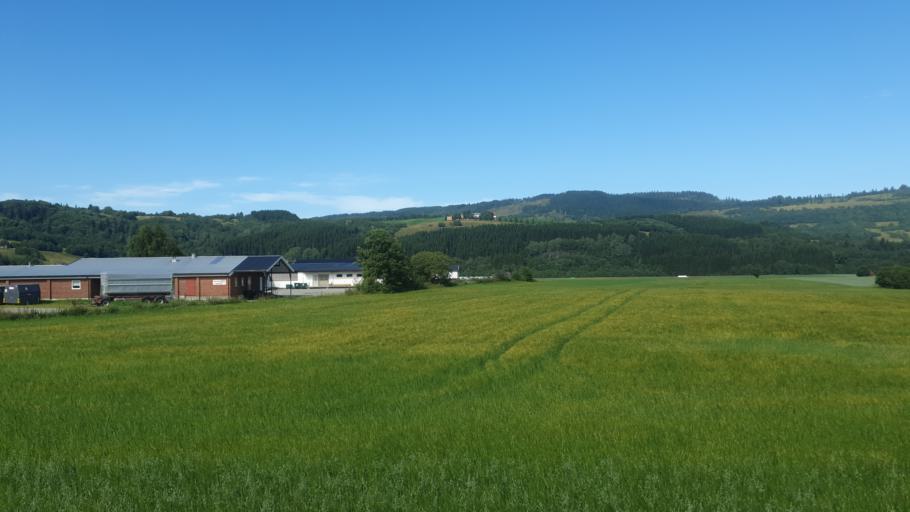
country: NO
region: Sor-Trondelag
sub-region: Orkdal
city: Orkanger
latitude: 63.2685
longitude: 9.8159
